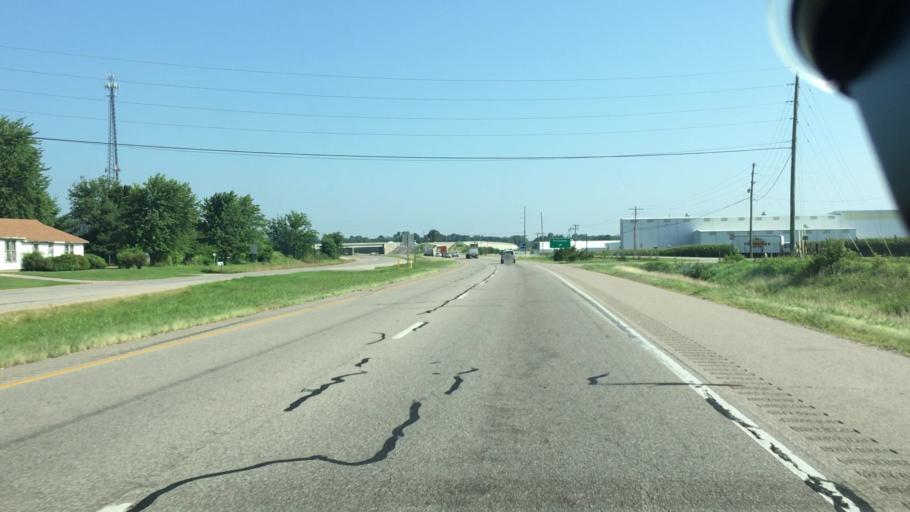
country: US
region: Indiana
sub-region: Gibson County
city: Princeton
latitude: 38.3070
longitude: -87.5673
